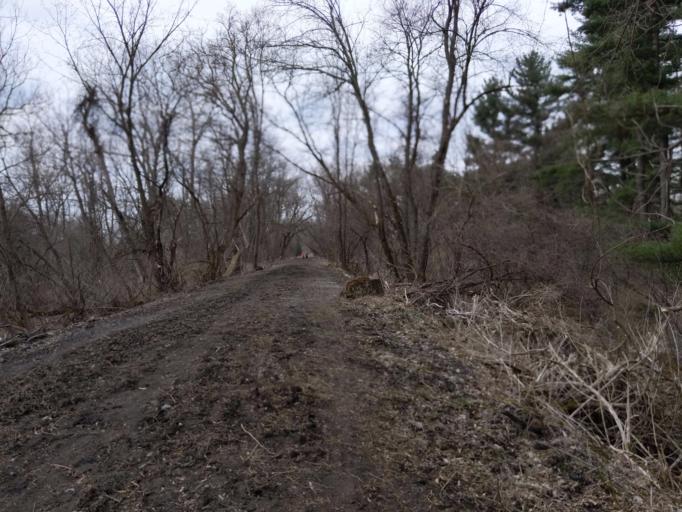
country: US
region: New York
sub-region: Tompkins County
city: Dryden
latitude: 42.4989
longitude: -76.3319
